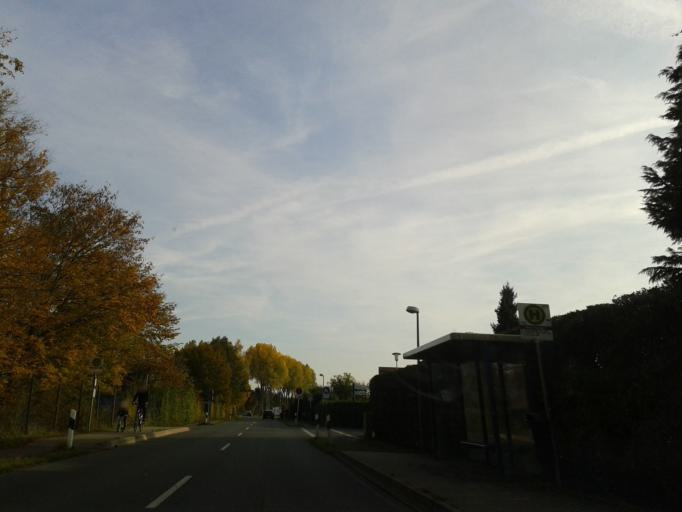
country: DE
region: North Rhine-Westphalia
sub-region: Regierungsbezirk Detmold
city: Hovelhof
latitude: 51.7526
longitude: 8.6662
